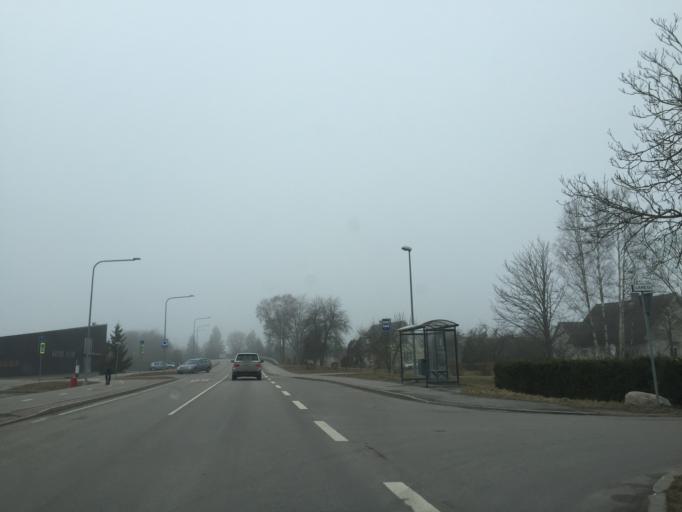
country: EE
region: Saare
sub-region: Kuressaare linn
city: Kuressaare
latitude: 58.2286
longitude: 22.3856
